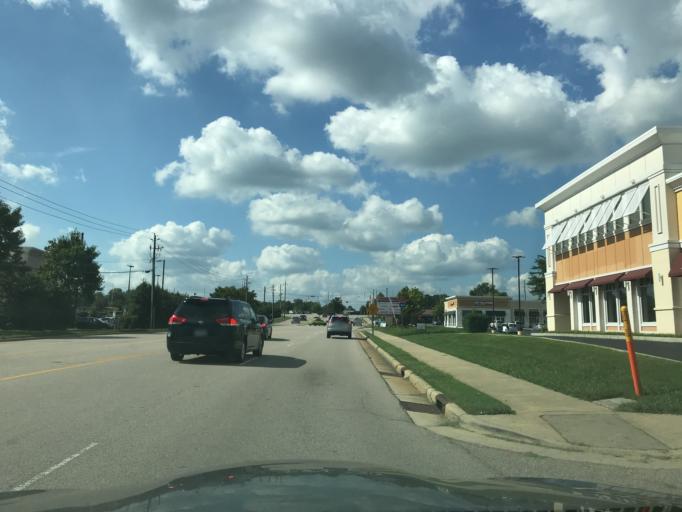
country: US
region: North Carolina
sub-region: Wake County
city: Raleigh
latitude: 35.8698
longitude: -78.5781
